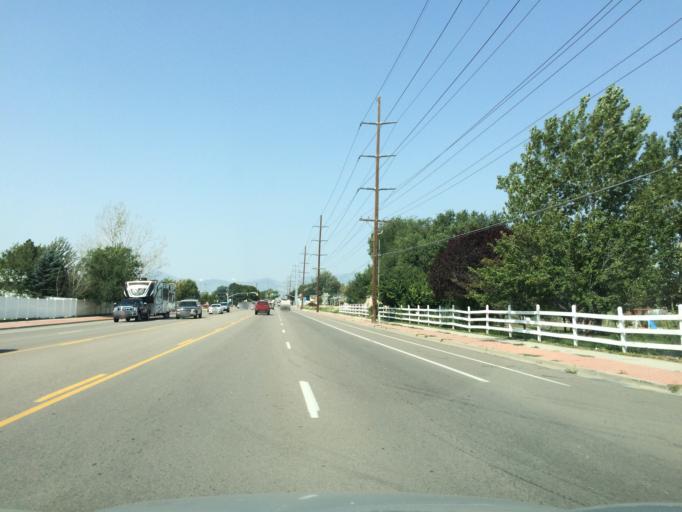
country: US
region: Utah
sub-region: Salt Lake County
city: South Jordan Heights
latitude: 40.5878
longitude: -111.9638
